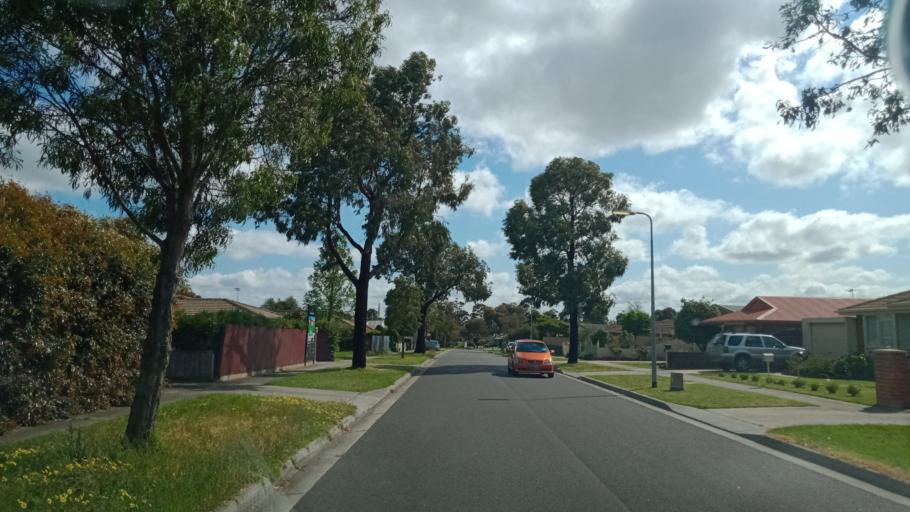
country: AU
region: Victoria
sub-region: Frankston
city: Carrum Downs
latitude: -38.0891
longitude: 145.1889
